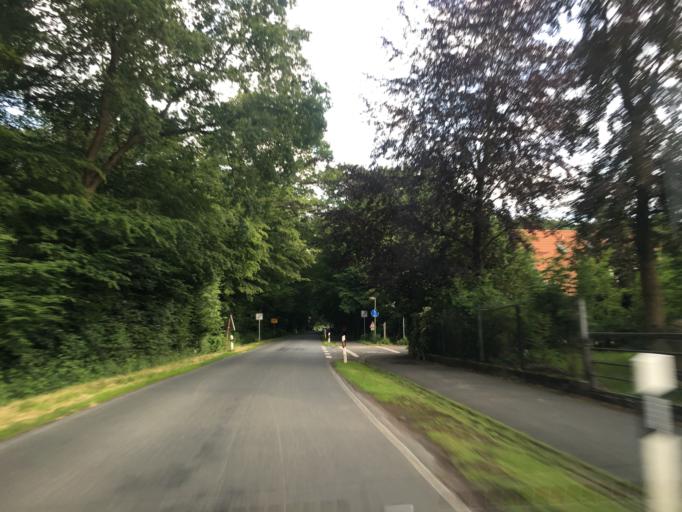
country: DE
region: North Rhine-Westphalia
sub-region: Regierungsbezirk Munster
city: Havixbeck
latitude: 51.9957
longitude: 7.4656
